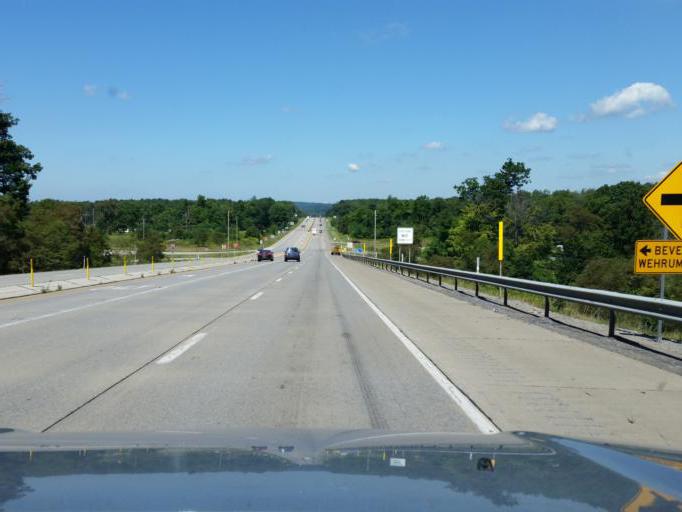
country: US
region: Pennsylvania
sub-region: Cambria County
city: Vinco
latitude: 40.4440
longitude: -78.9693
